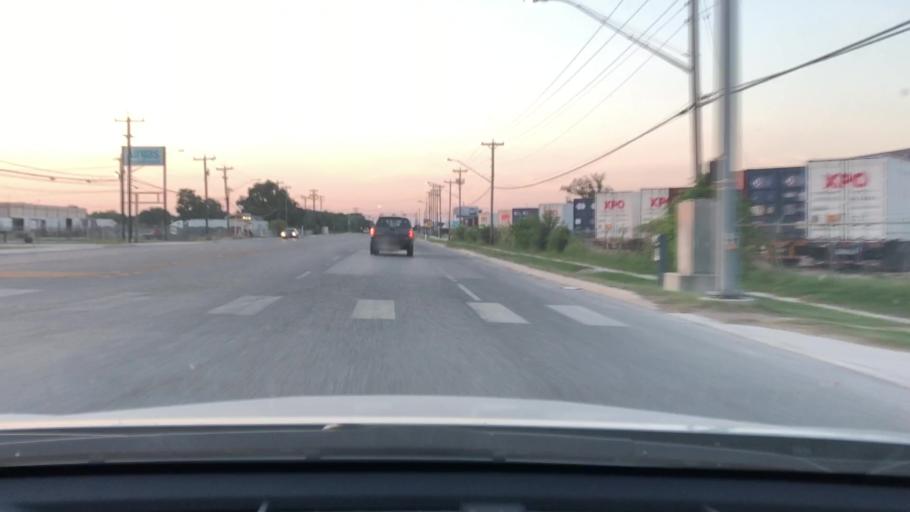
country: US
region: Texas
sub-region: Bexar County
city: Kirby
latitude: 29.4357
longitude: -98.4055
